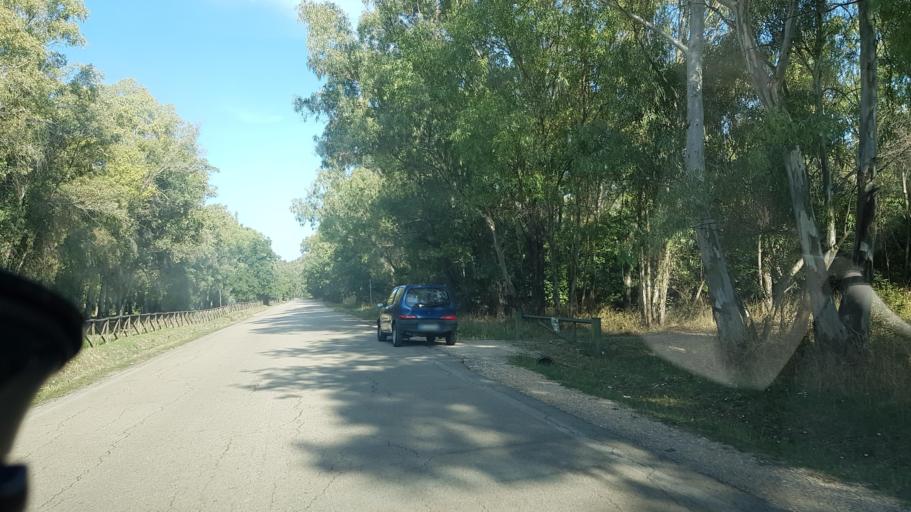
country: IT
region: Apulia
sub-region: Provincia di Foggia
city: Carapelle
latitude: 41.3854
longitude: 15.6448
